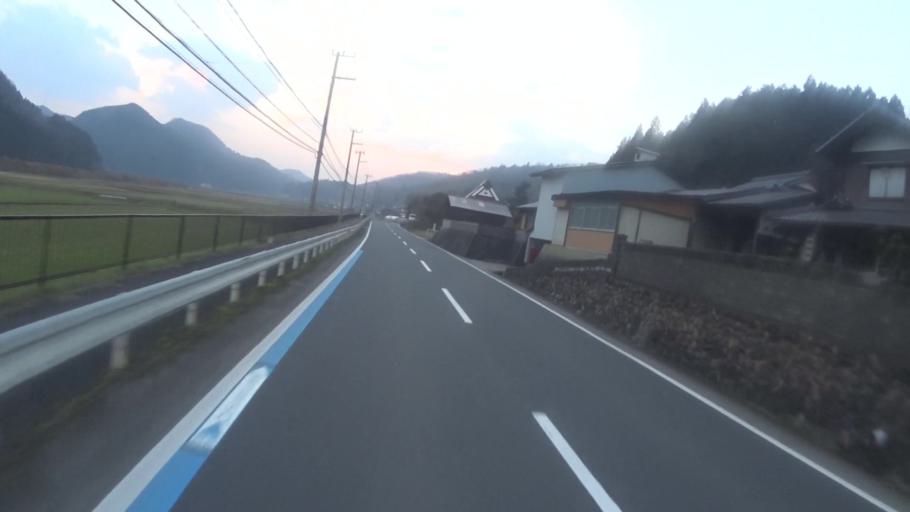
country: JP
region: Kyoto
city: Ayabe
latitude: 35.3317
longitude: 135.3406
